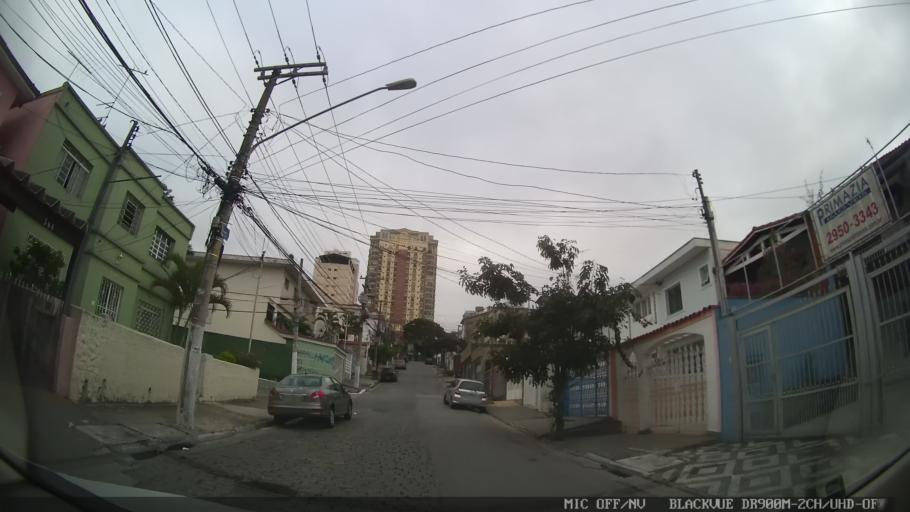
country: BR
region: Sao Paulo
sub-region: Sao Paulo
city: Sao Paulo
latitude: -23.4904
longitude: -46.6196
